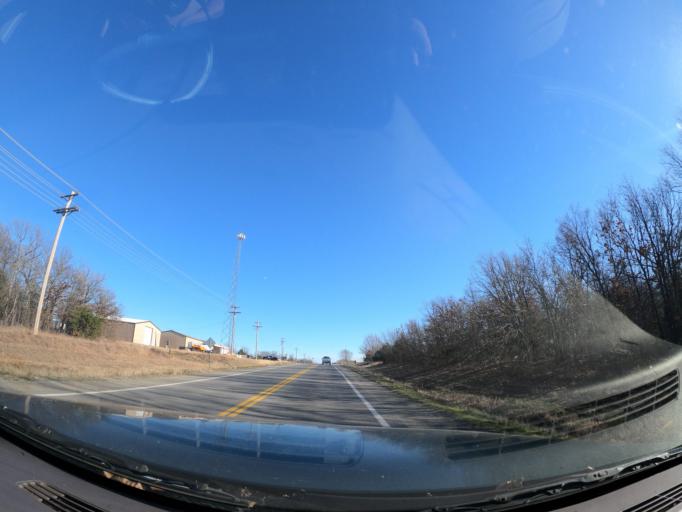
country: US
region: Oklahoma
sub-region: Pittsburg County
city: Longtown
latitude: 35.2366
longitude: -95.4663
